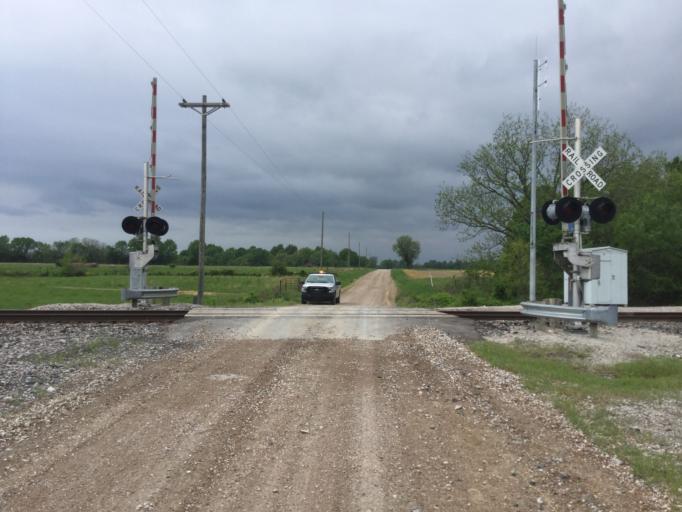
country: US
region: Kansas
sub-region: Labette County
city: Oswego
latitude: 37.1062
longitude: -95.1181
